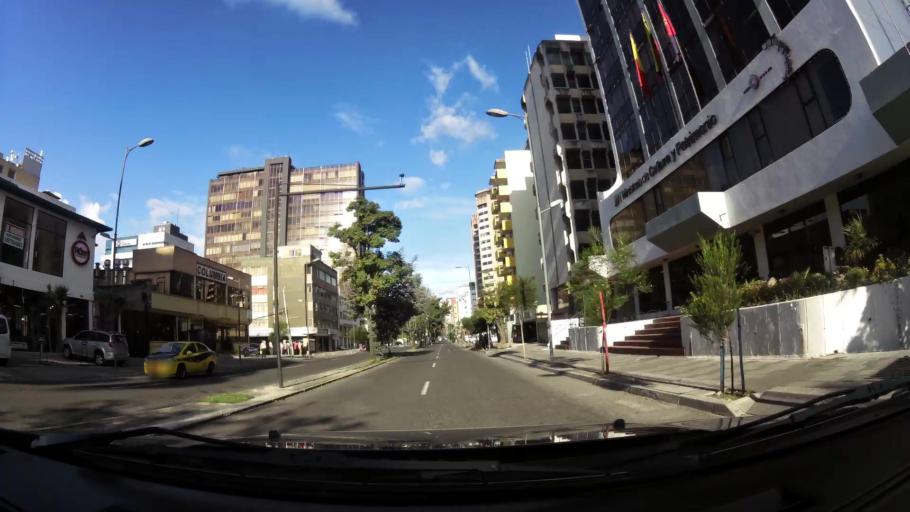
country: EC
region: Pichincha
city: Quito
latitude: -0.2006
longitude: -78.4901
